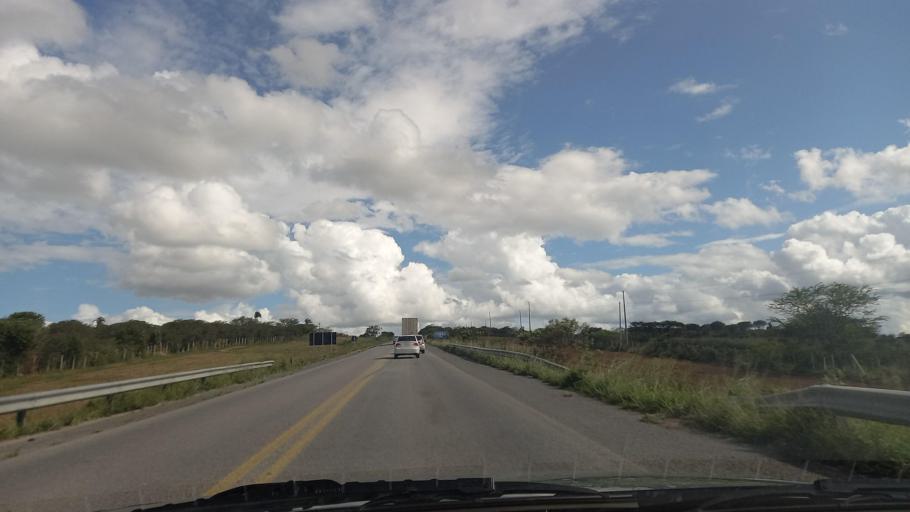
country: BR
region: Pernambuco
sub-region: Sao Joao
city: Sao Joao
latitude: -8.7980
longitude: -36.4380
